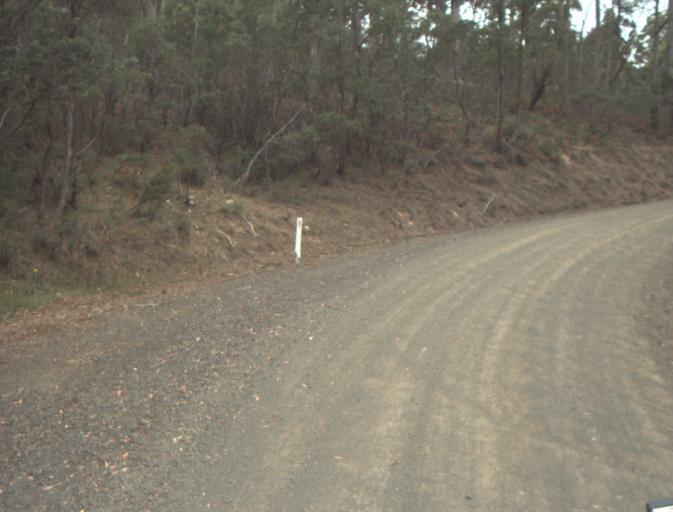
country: AU
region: Tasmania
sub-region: Northern Midlands
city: Evandale
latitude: -41.4863
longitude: 147.5404
